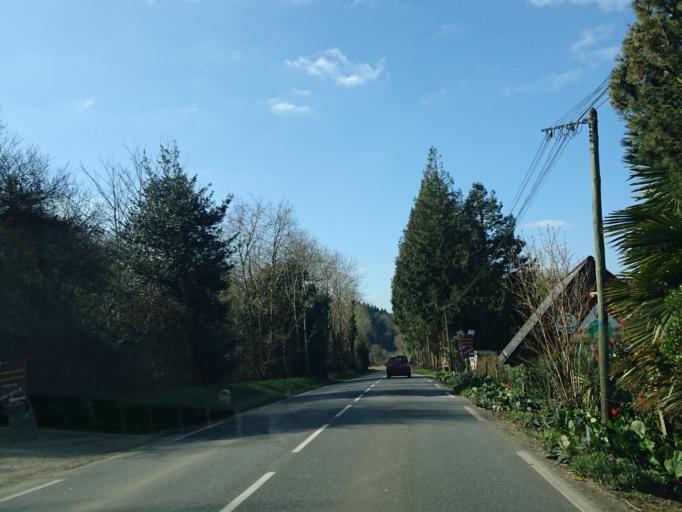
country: FR
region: Brittany
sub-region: Departement du Finistere
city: Logonna-Daoulas
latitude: 48.2796
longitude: -4.2759
